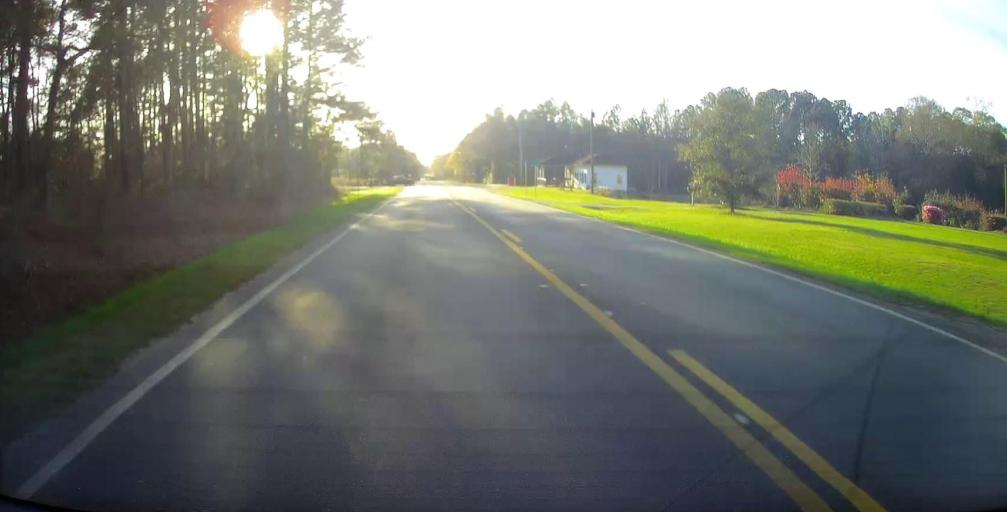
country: US
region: Georgia
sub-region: Evans County
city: Claxton
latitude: 32.1523
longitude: -81.8351
